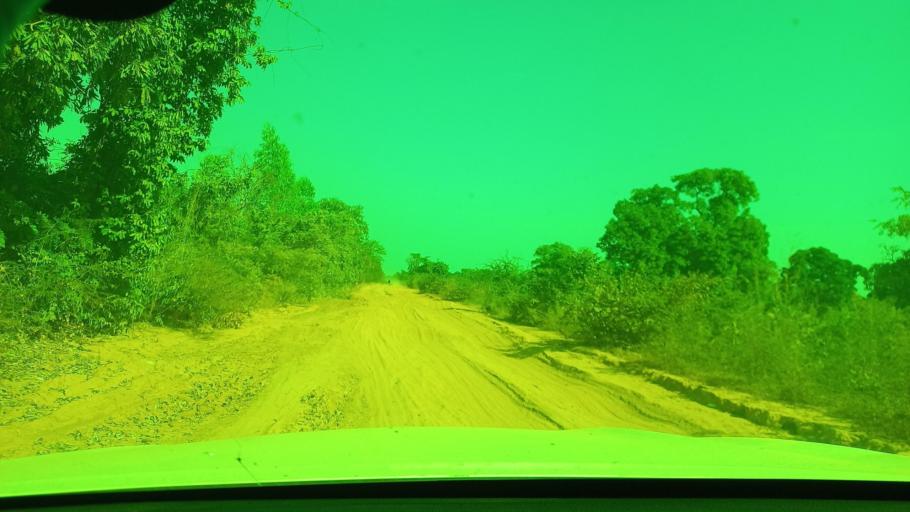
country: ML
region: Bamako
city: Bamako
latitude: 12.3972
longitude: -7.9897
